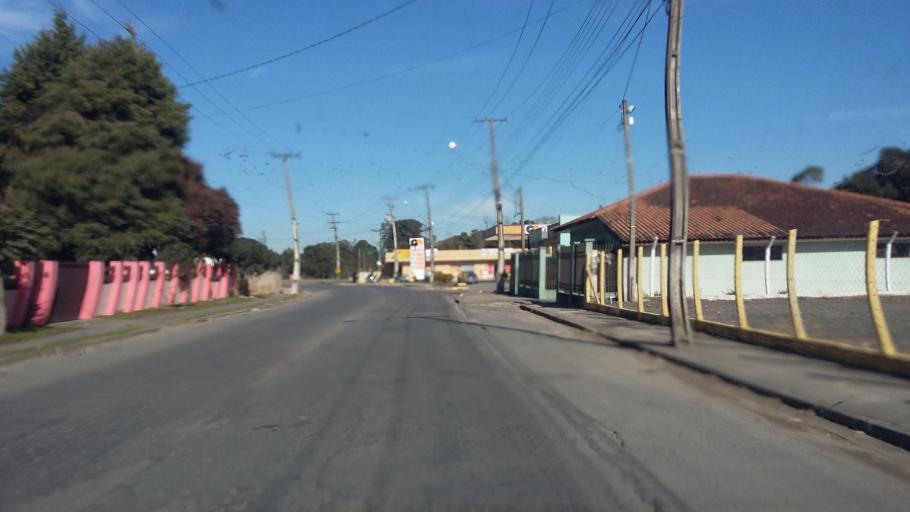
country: BR
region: Parana
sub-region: Campo Largo
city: Campo Largo
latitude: -25.4672
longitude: -49.5655
